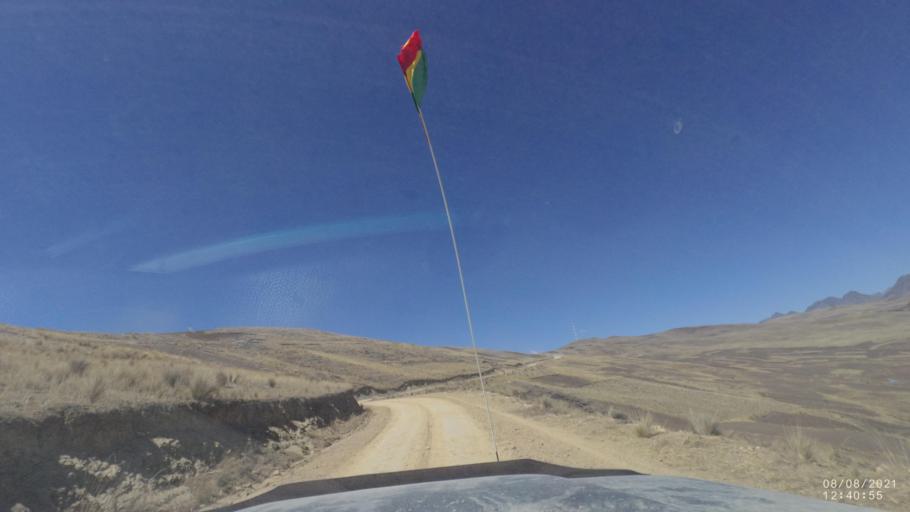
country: BO
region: Cochabamba
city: Colchani
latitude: -16.8312
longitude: -66.6219
